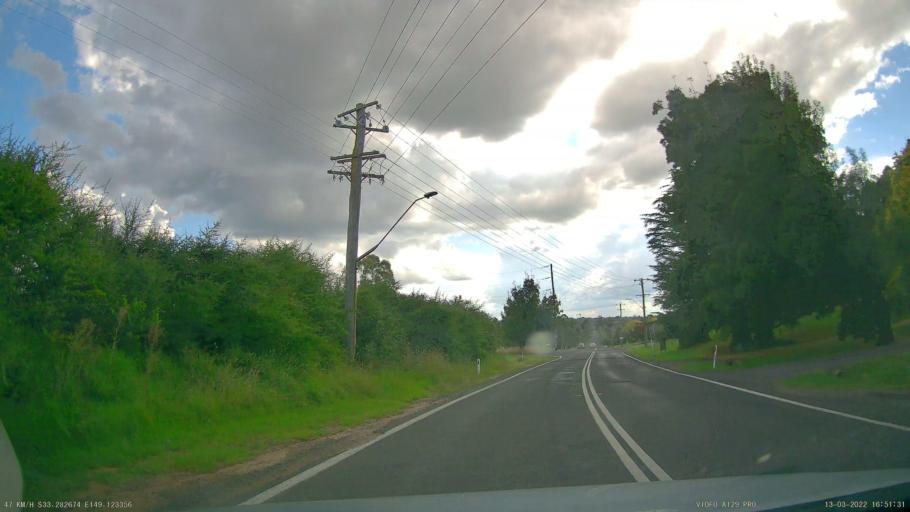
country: AU
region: New South Wales
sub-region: Orange Municipality
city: Orange
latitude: -33.2827
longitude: 149.1232
